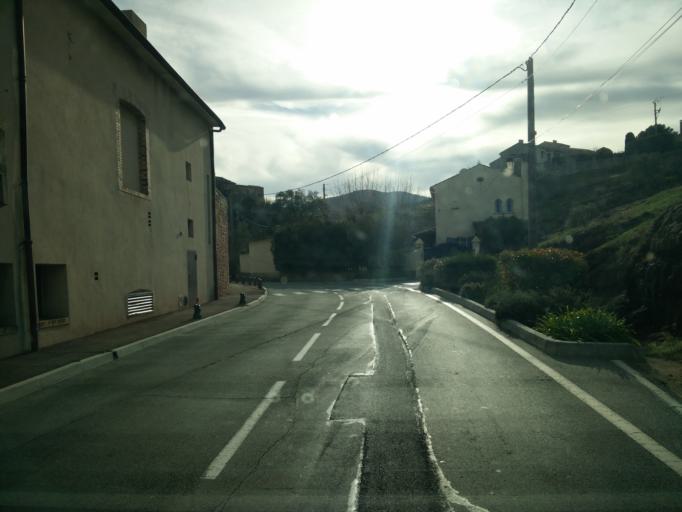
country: FR
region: Provence-Alpes-Cote d'Azur
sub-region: Departement du Var
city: Roquebrune-sur-Argens
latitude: 43.4452
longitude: 6.6361
